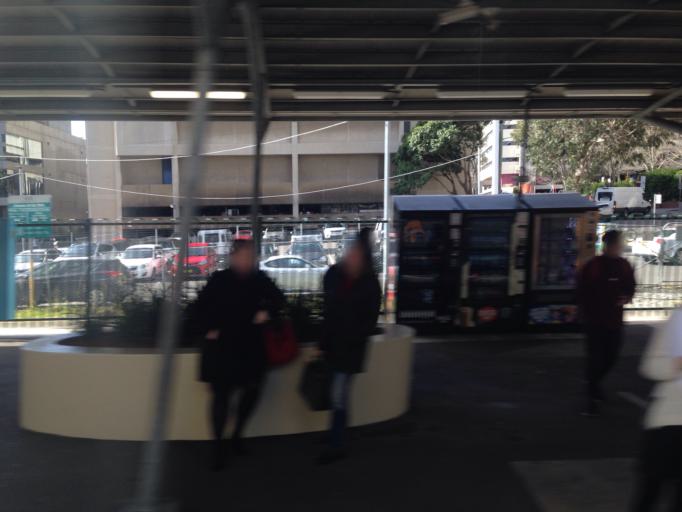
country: AU
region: New South Wales
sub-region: North Sydney
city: St Leonards
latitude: -33.8216
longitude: 151.1940
